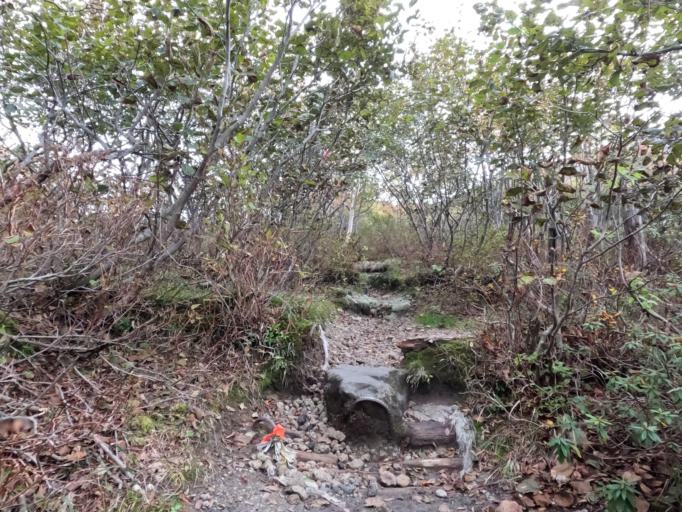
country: JP
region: Hokkaido
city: Shiraoi
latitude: 42.6985
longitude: 141.3912
